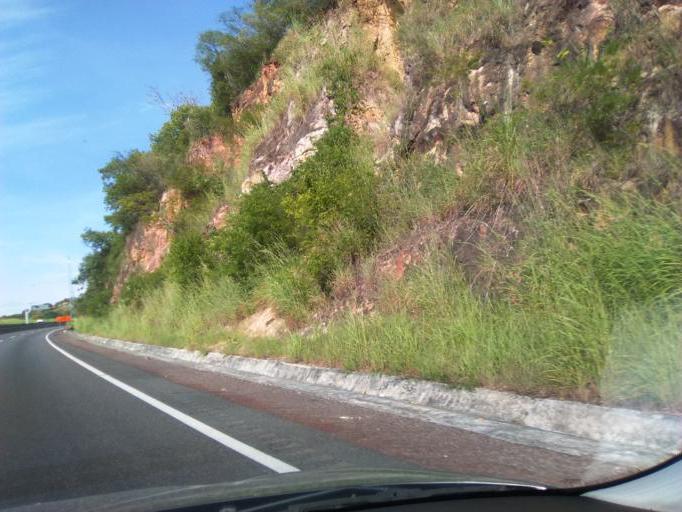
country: MX
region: Morelos
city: Tilzapotla
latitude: 18.3862
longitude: -99.1740
